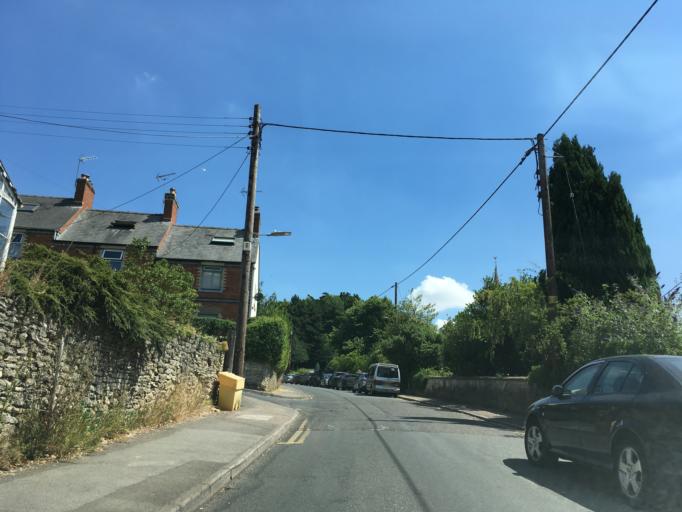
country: GB
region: England
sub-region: Gloucestershire
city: Stroud
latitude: 51.7426
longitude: -2.2017
